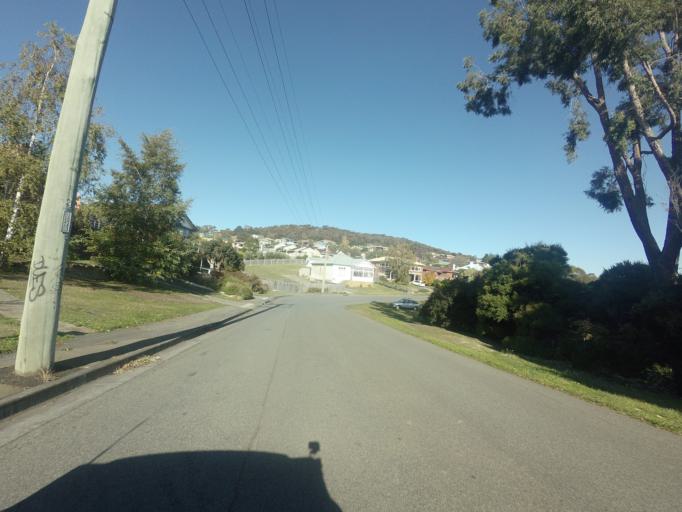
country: AU
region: Tasmania
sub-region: Clarence
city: Lindisfarne
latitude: -42.8643
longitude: 147.3560
